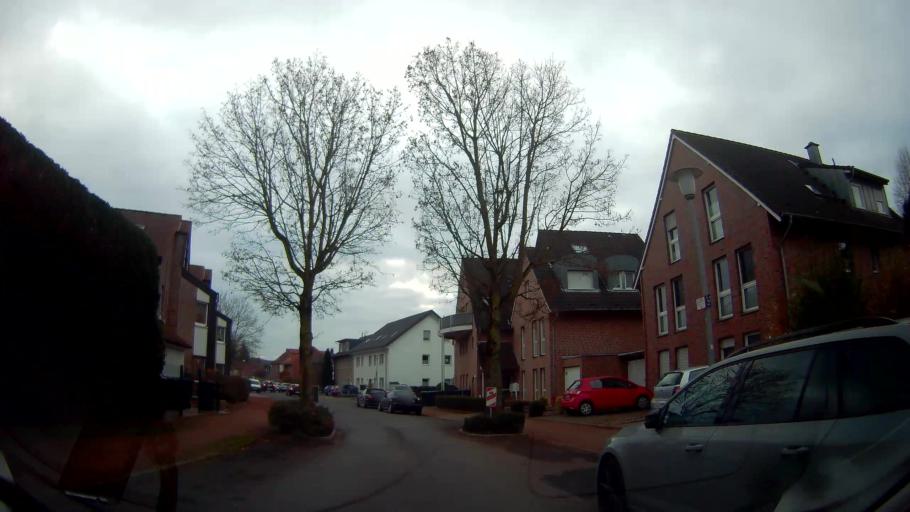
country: DE
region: North Rhine-Westphalia
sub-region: Regierungsbezirk Munster
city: Haltern
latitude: 51.7476
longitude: 7.1881
